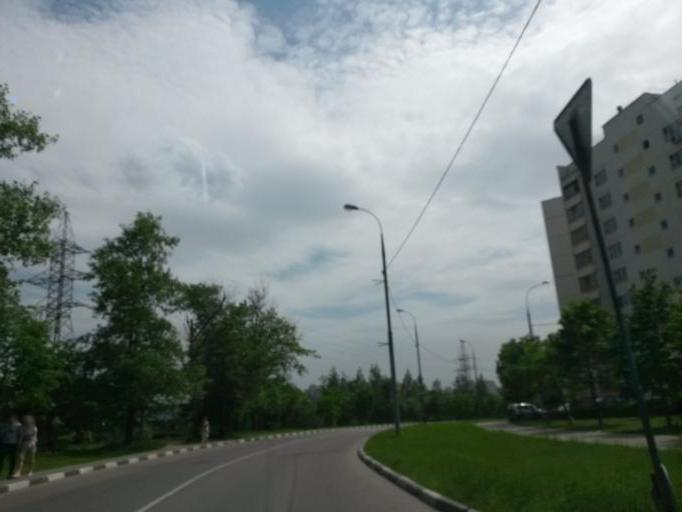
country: RU
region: Moskovskaya
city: Kommunarka
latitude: 55.5434
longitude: 37.5274
